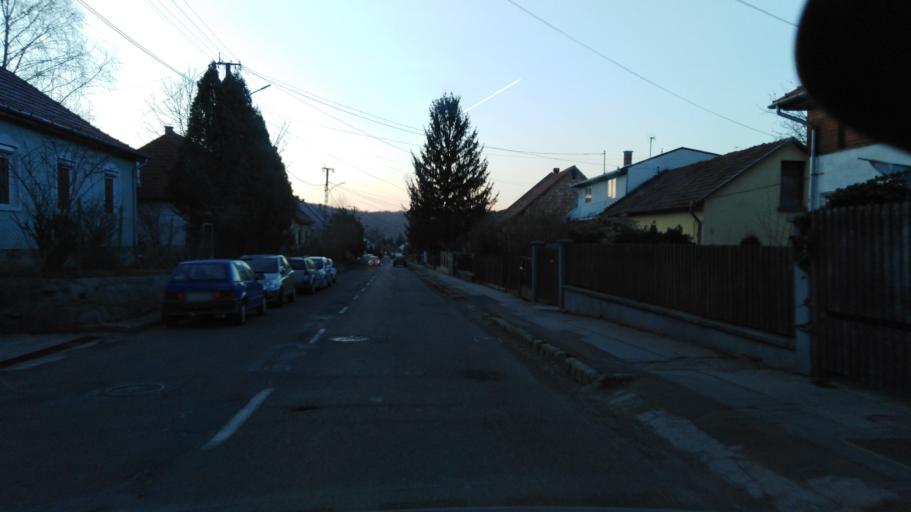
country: HU
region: Nograd
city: Salgotarjan
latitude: 48.0904
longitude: 19.8092
